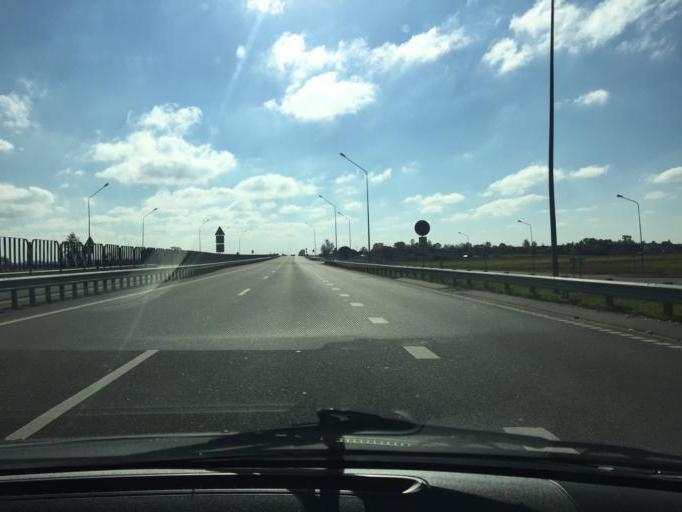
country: BY
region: Minsk
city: Slutsk
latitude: 53.1494
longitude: 27.5517
